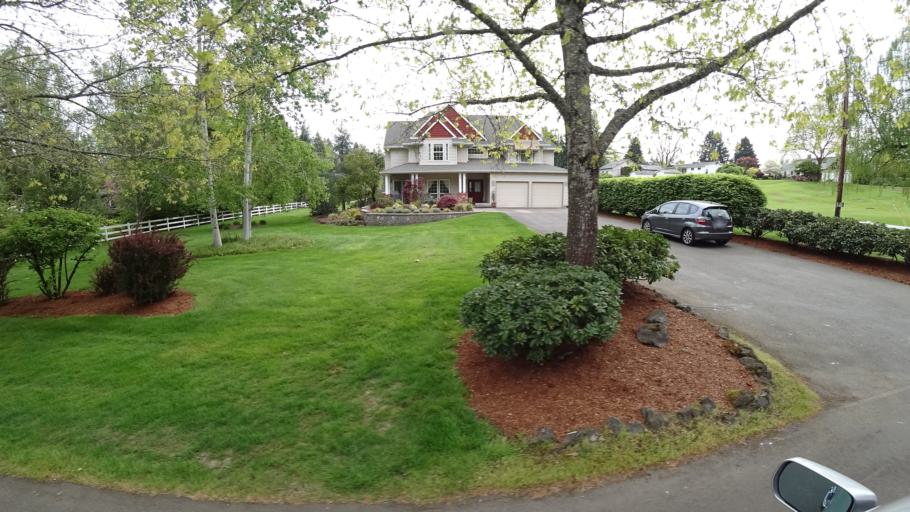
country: US
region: Oregon
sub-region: Washington County
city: Hillsboro
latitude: 45.5292
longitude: -123.0033
